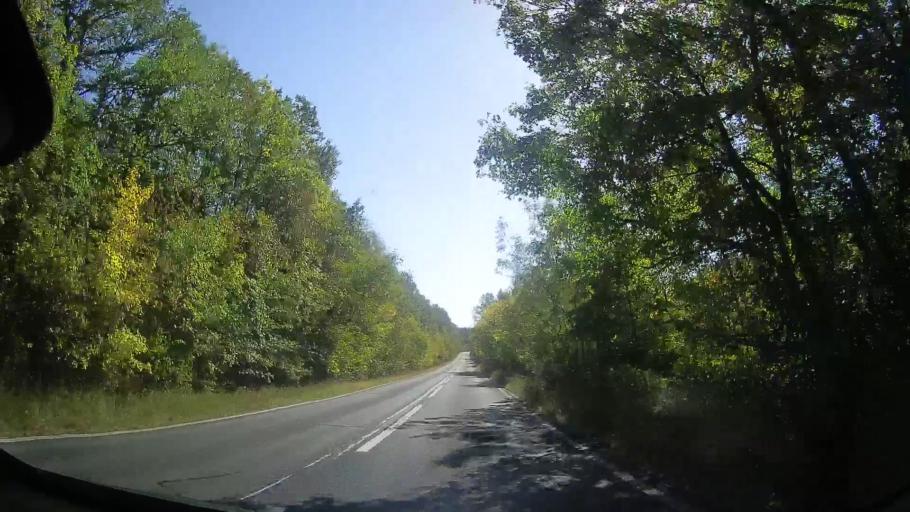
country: RO
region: Timis
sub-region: Comuna Barna
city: Barna
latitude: 45.7404
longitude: 21.9956
